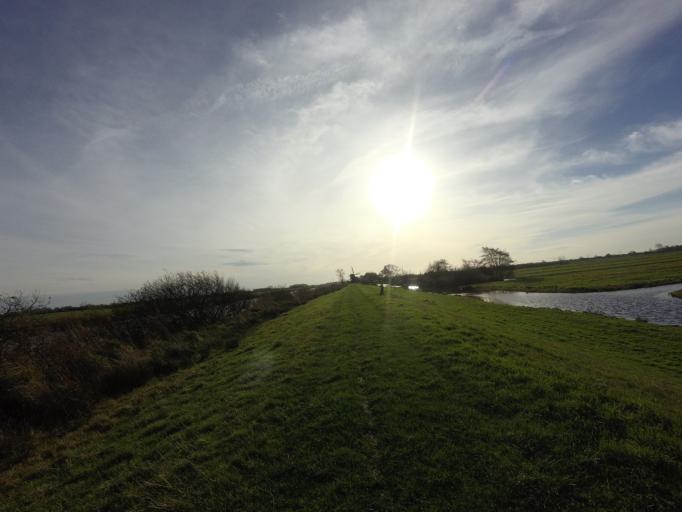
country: NL
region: South Holland
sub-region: Gemeente Vlist
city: Haastrecht
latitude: 52.0361
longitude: 4.7864
